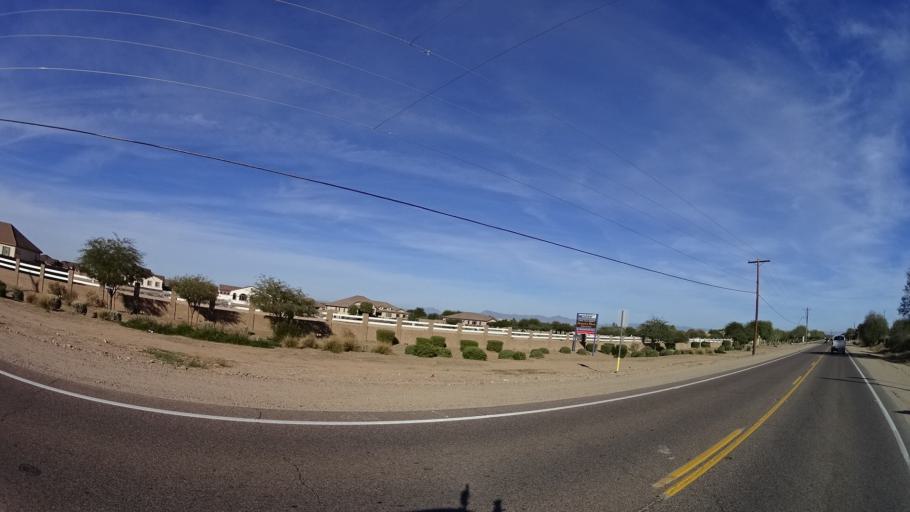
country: US
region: Arizona
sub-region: Maricopa County
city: Queen Creek
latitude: 33.2195
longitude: -111.6622
